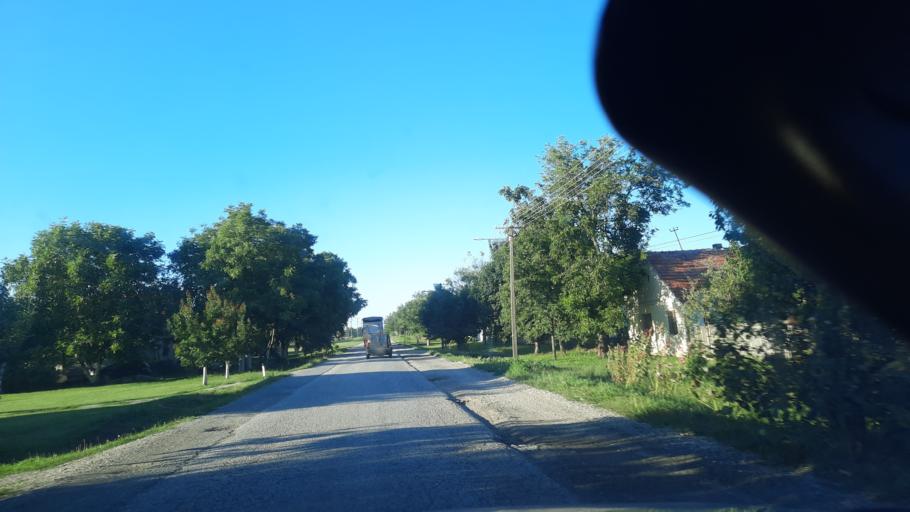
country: RS
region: Autonomna Pokrajina Vojvodina
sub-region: Sremski Okrug
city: Irig
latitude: 45.1147
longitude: 19.9352
